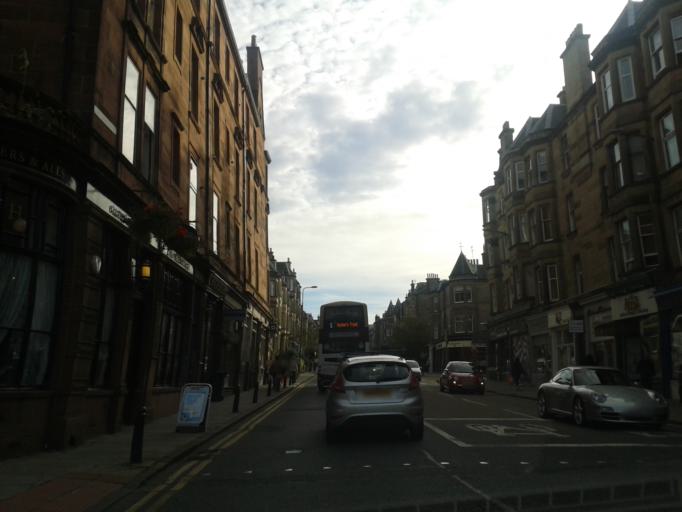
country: GB
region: Scotland
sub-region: Edinburgh
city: Edinburgh
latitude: 55.9249
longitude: -3.2097
